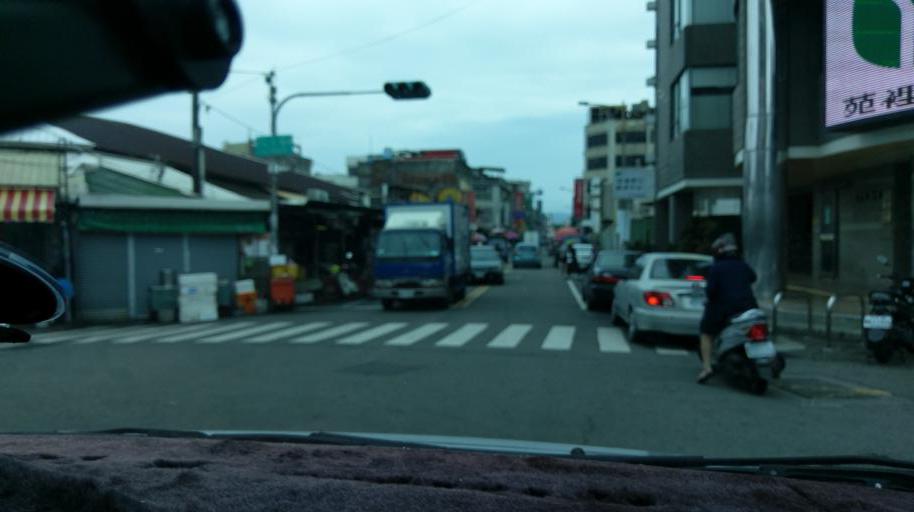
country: TW
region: Taiwan
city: Fengyuan
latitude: 24.4431
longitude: 120.6525
